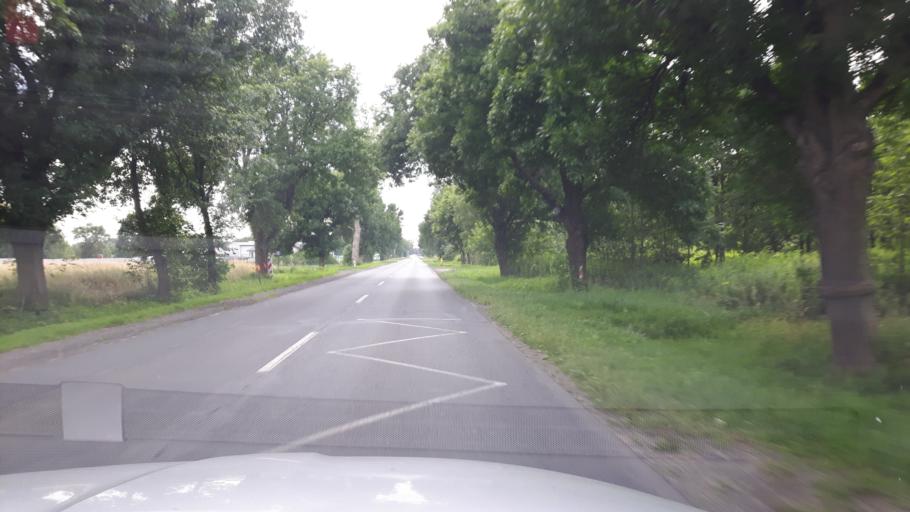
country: PL
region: Masovian Voivodeship
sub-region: Powiat wolominski
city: Duczki
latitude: 52.3673
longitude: 21.3044
